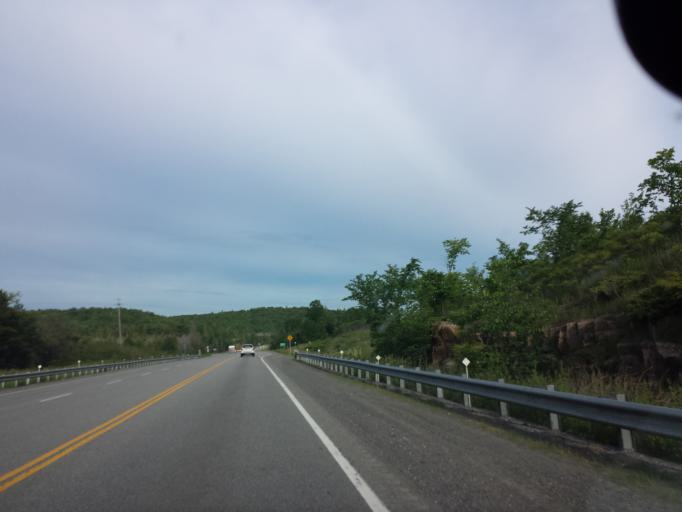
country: CA
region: Ontario
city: Renfrew
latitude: 45.4458
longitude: -76.5814
